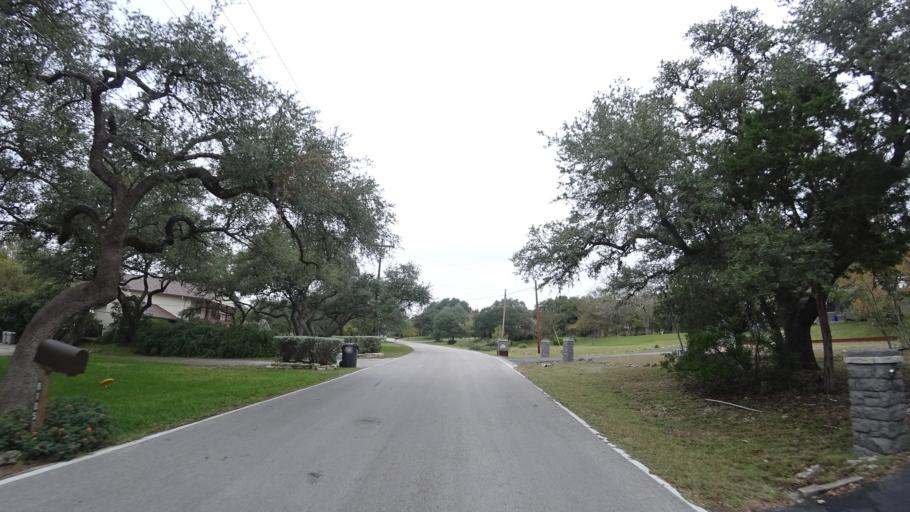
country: US
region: Texas
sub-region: Travis County
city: Barton Creek
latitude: 30.2243
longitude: -97.9028
